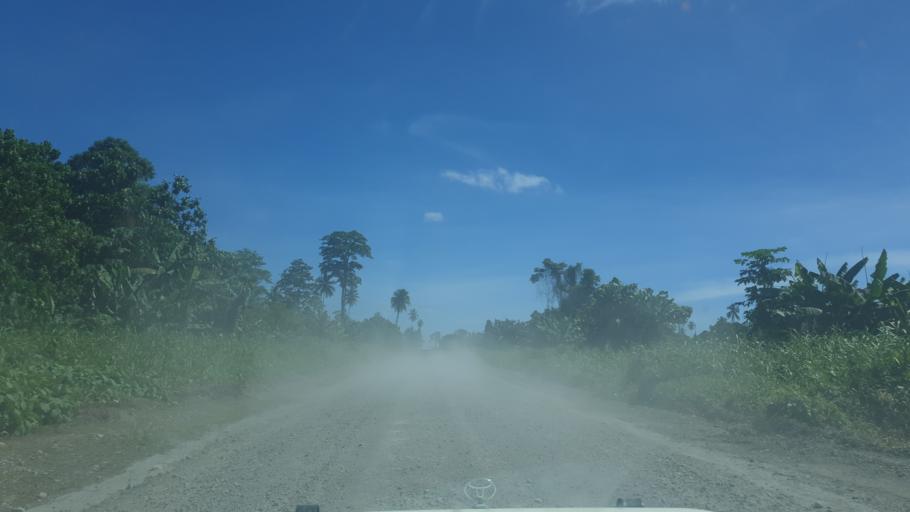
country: PG
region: Bougainville
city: Arawa
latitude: -5.9839
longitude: 155.3557
